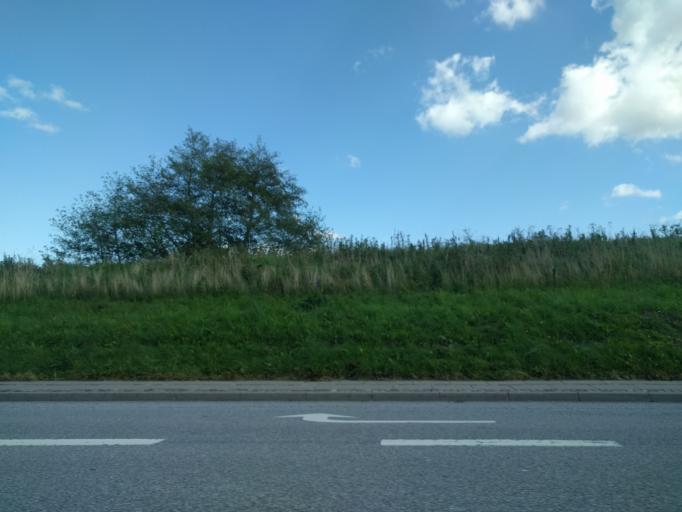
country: DK
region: Central Jutland
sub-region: Skive Kommune
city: Skive
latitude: 56.5916
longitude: 9.0283
